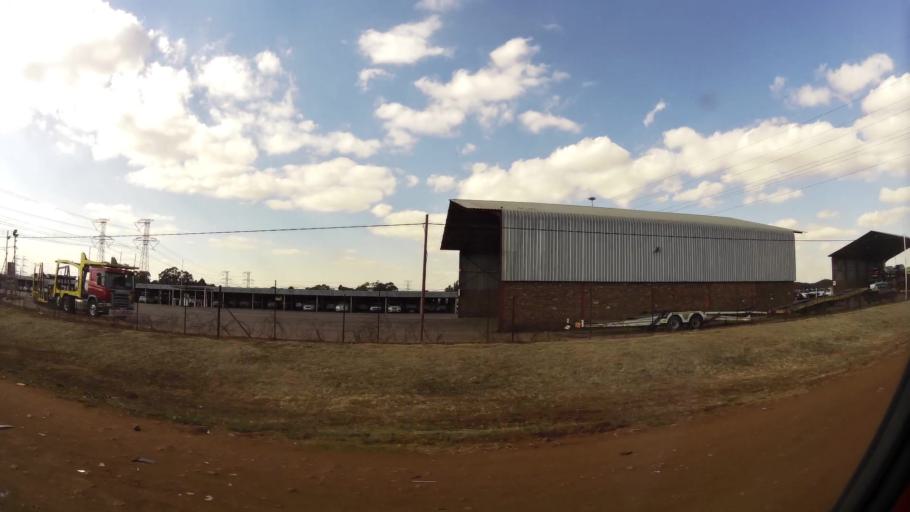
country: ZA
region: Gauteng
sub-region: Ekurhuleni Metropolitan Municipality
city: Tembisa
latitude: -26.0158
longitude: 28.2549
